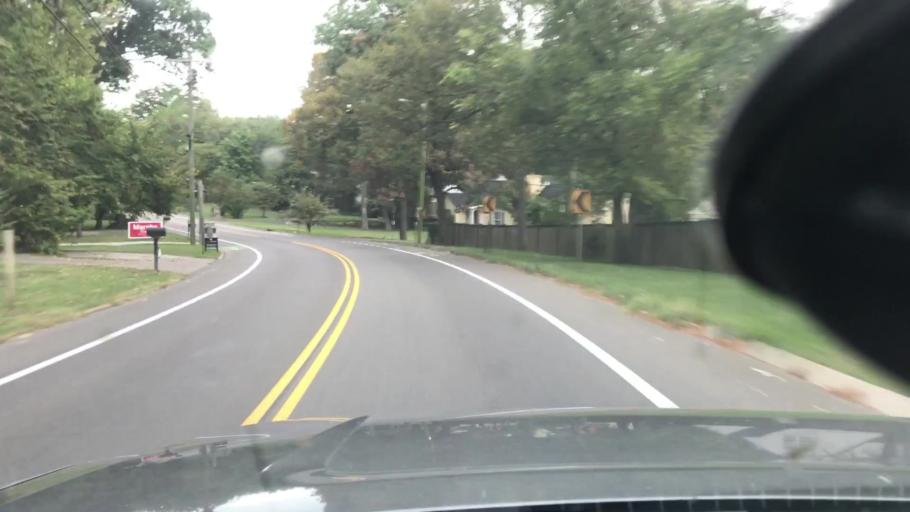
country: US
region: Tennessee
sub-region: Davidson County
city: Belle Meade
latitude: 36.1170
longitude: -86.8402
